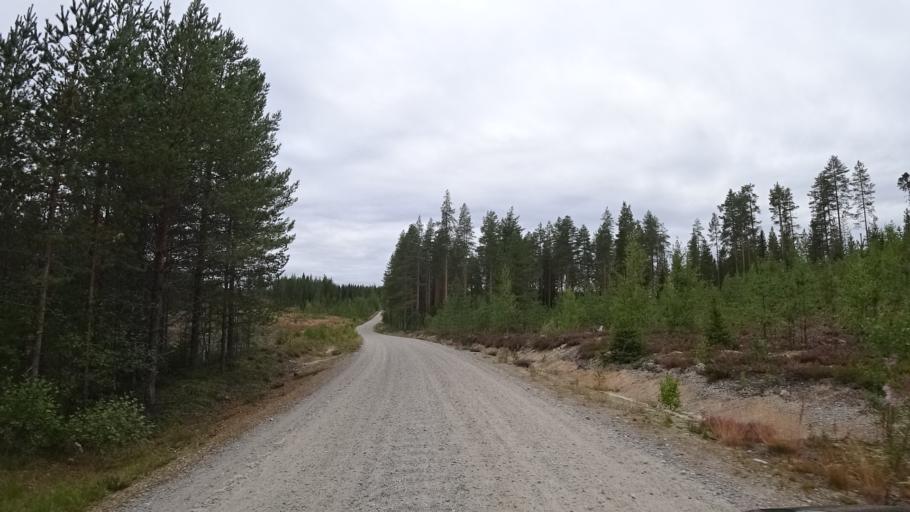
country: FI
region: North Karelia
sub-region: Joensuu
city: Ilomantsi
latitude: 63.1551
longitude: 30.6346
